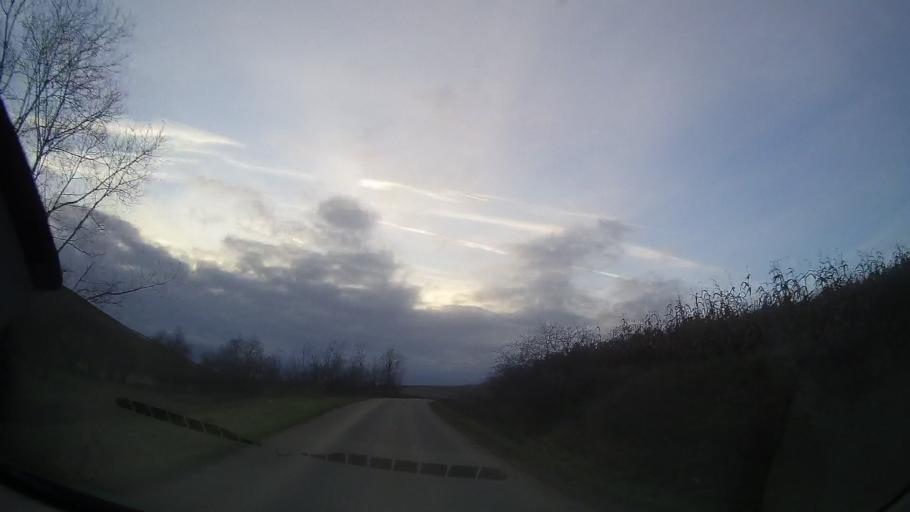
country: RO
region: Cluj
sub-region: Comuna Geaca
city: Geaca
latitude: 46.8531
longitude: 24.0661
